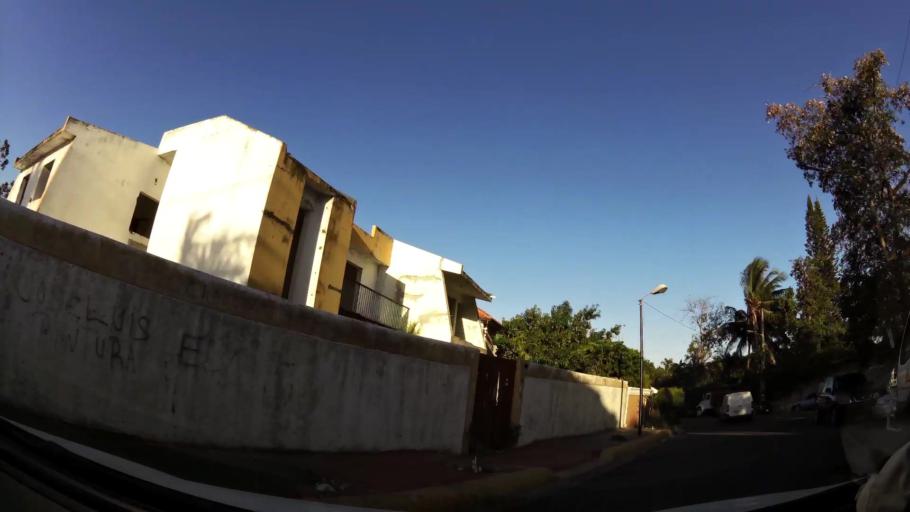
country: DO
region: Nacional
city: Santo Domingo
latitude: 18.4907
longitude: -69.9671
